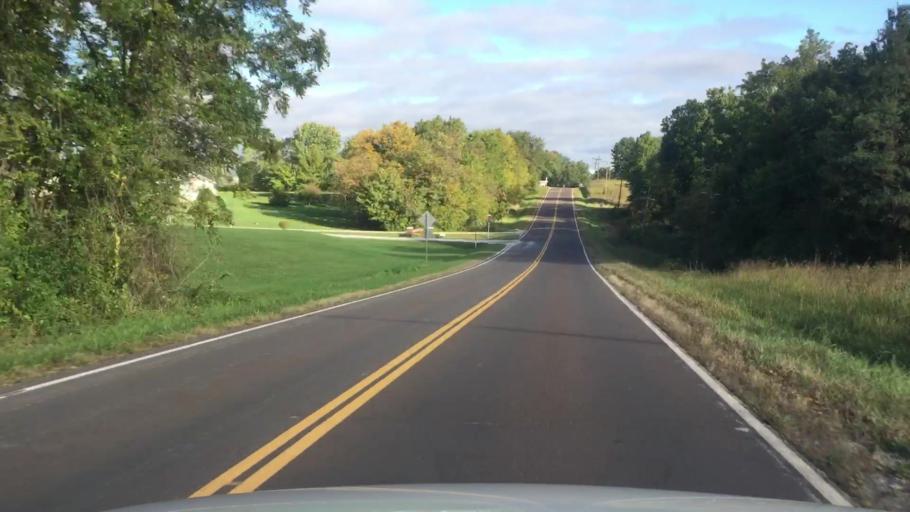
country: US
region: Missouri
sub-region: Howard County
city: New Franklin
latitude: 39.0361
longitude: -92.7437
